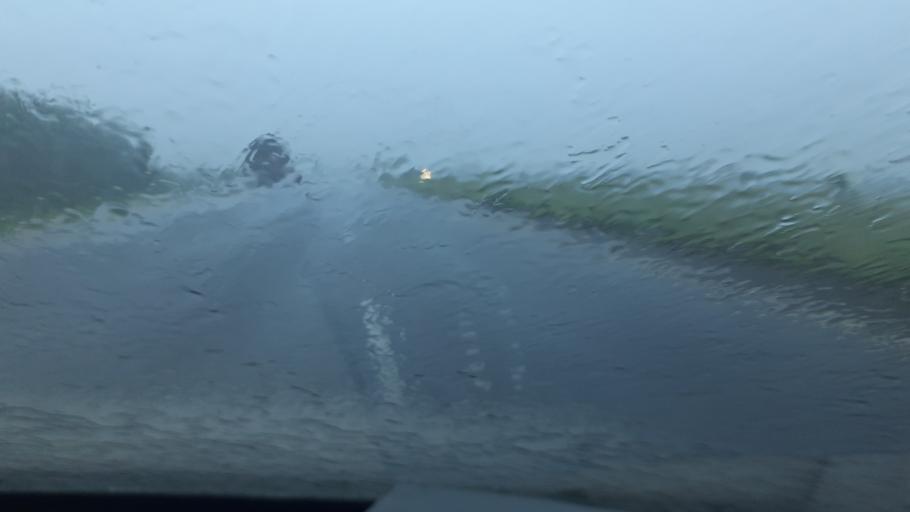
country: IN
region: Tamil Nadu
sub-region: Virudhunagar
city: Virudunagar
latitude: 9.4876
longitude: 77.9414
